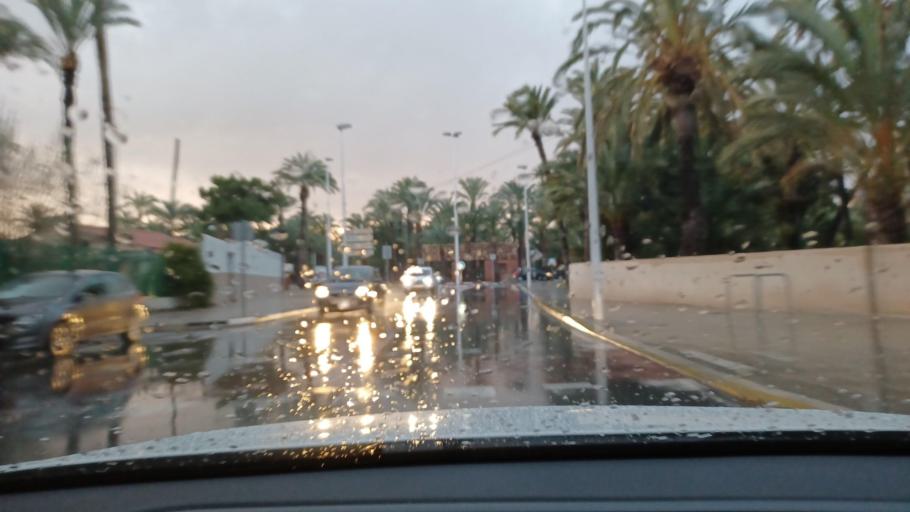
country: ES
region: Valencia
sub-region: Provincia de Alicante
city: Elche
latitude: 38.2583
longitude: -0.6930
